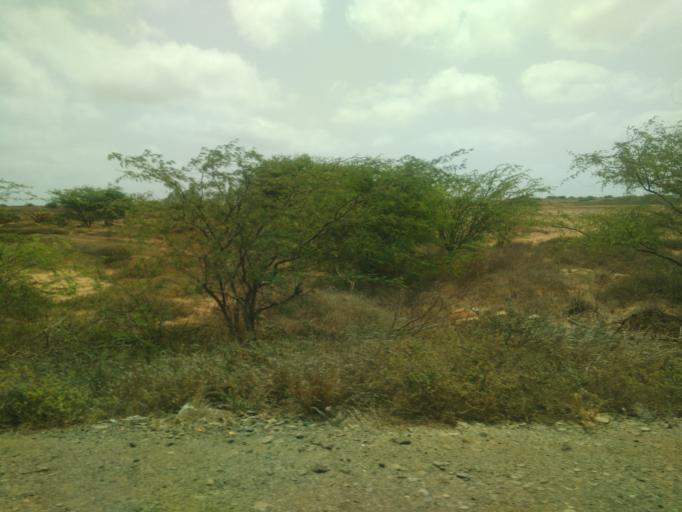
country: CV
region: Sal
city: Espargos
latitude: 16.6951
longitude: -22.9411
